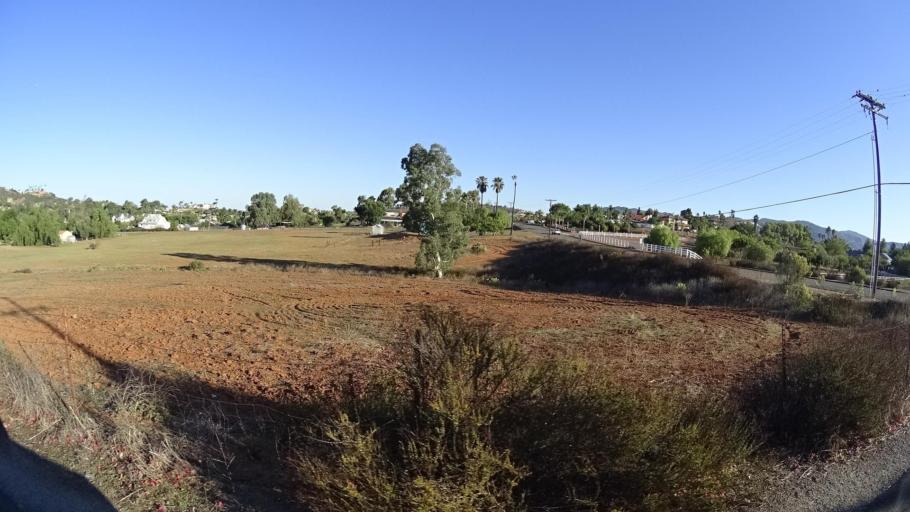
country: US
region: California
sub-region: San Diego County
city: Jamul
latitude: 32.7065
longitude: -116.8810
